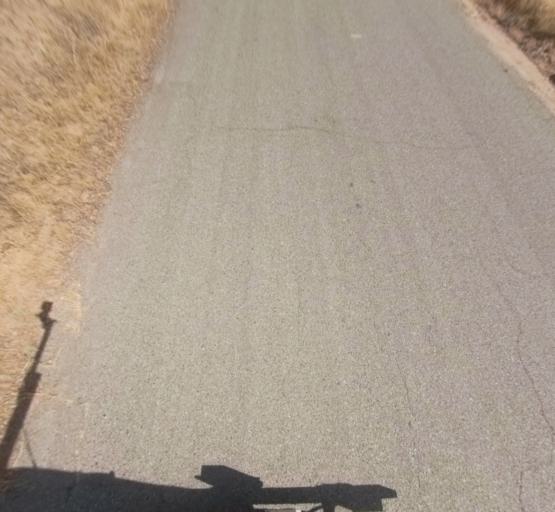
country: US
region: California
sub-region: Madera County
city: Yosemite Lakes
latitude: 37.1145
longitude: -119.6547
